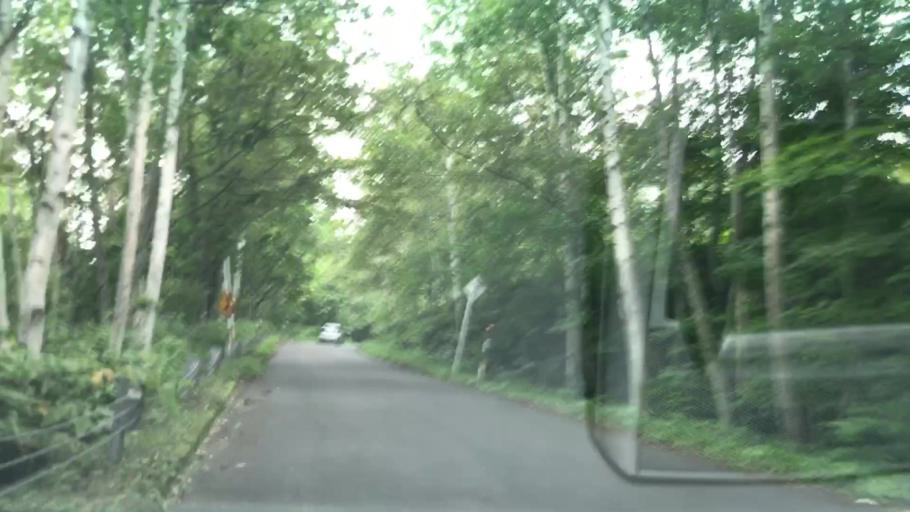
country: JP
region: Hokkaido
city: Yoichi
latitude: 43.1373
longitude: 140.8202
